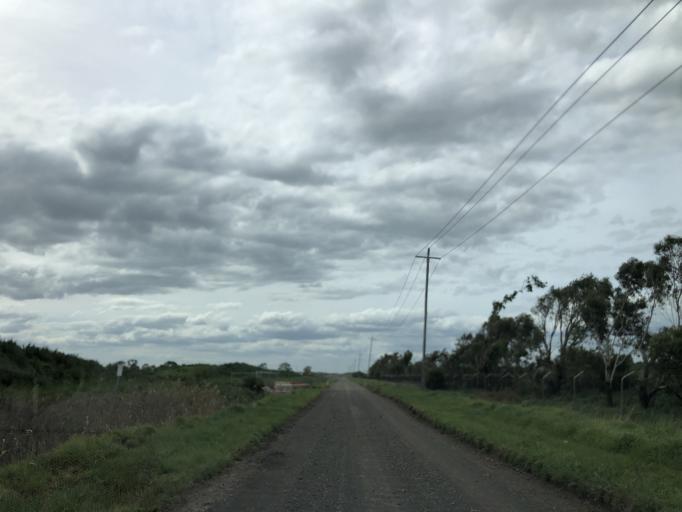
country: AU
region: Victoria
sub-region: Kingston
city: Patterson Lakes
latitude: -38.0747
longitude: 145.1659
